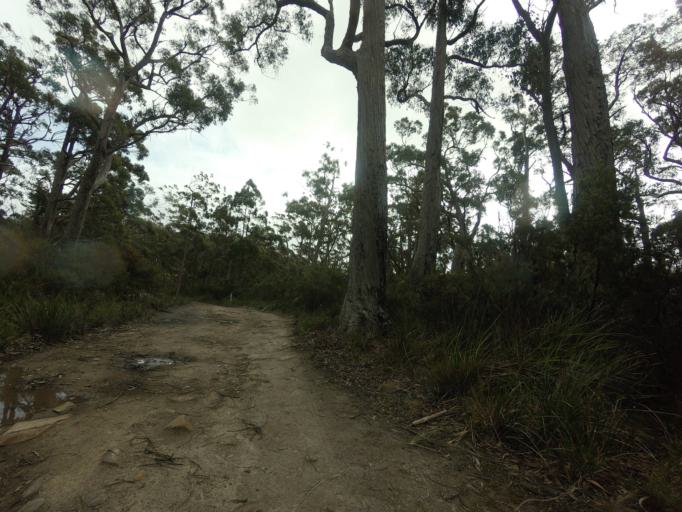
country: AU
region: Tasmania
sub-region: Huon Valley
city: Geeveston
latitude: -43.4732
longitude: 146.9342
